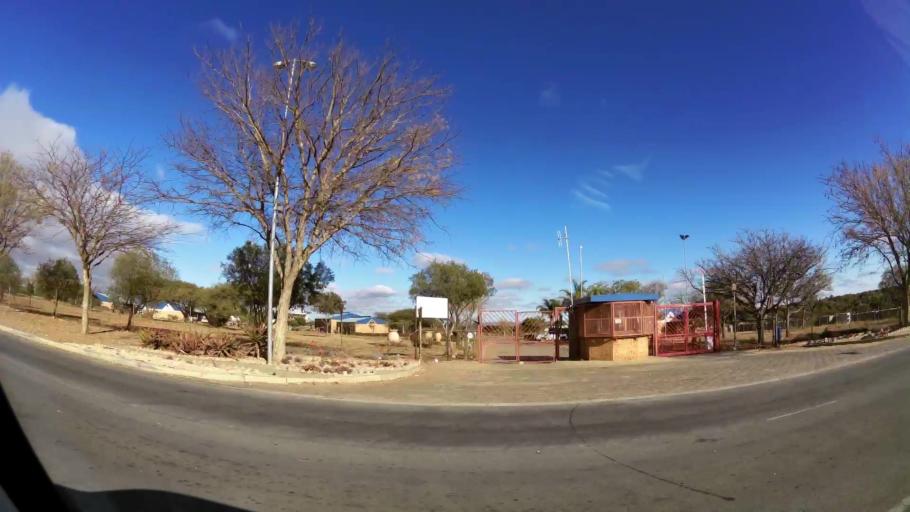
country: ZA
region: Limpopo
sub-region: Capricorn District Municipality
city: Polokwane
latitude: -23.9191
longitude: 29.4765
